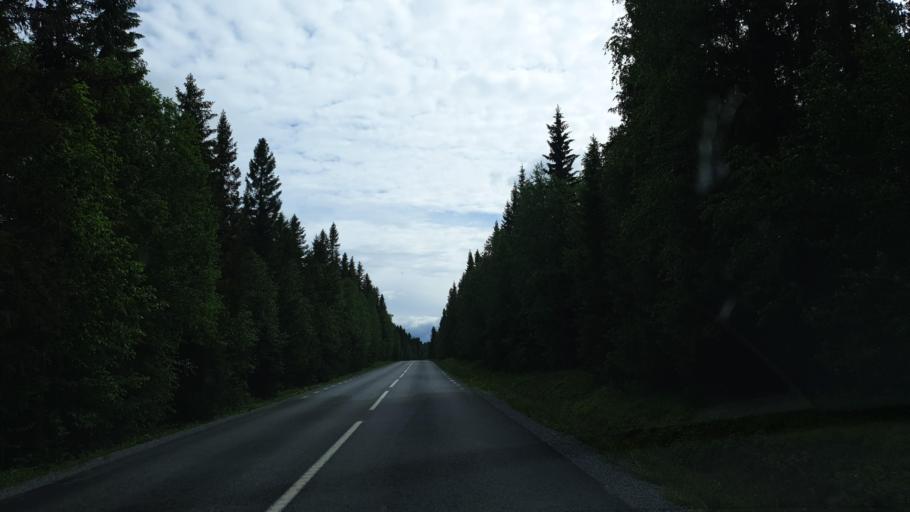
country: SE
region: Vaesterbotten
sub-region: Vilhelmina Kommun
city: Sjoberg
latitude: 64.6721
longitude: 16.2947
